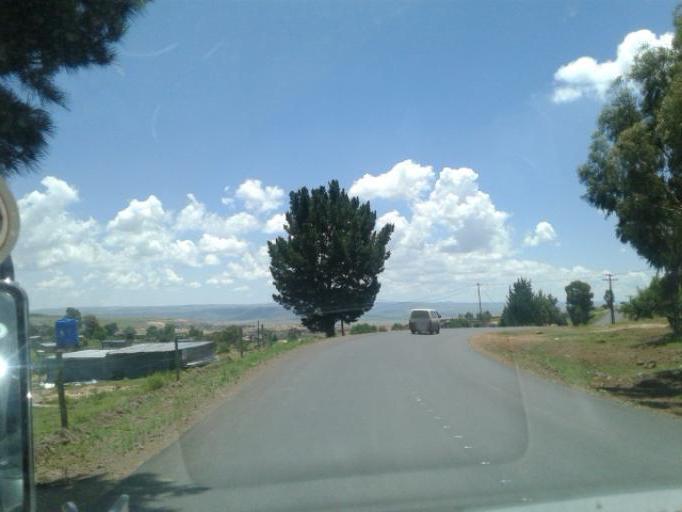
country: LS
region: Maseru
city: Maseru
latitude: -29.3246
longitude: 27.5856
